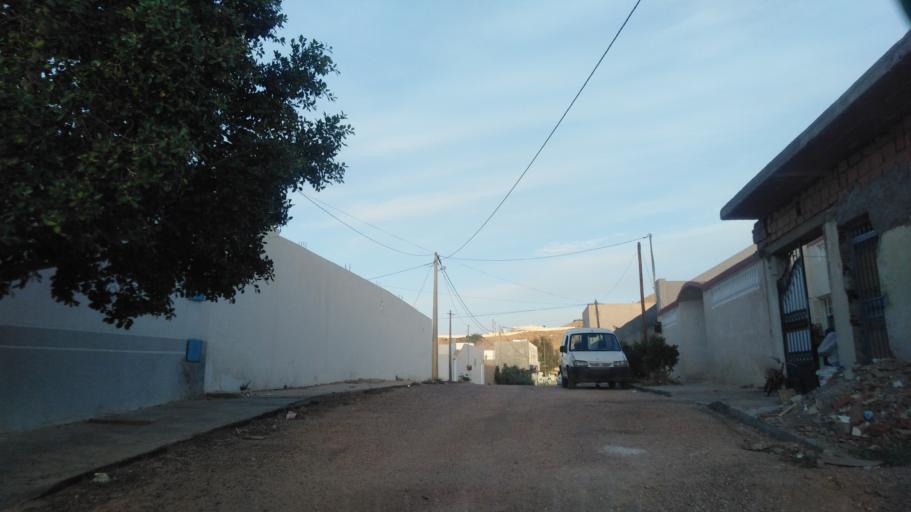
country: TN
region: Tataouine
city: Tataouine
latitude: 32.9418
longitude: 10.4590
